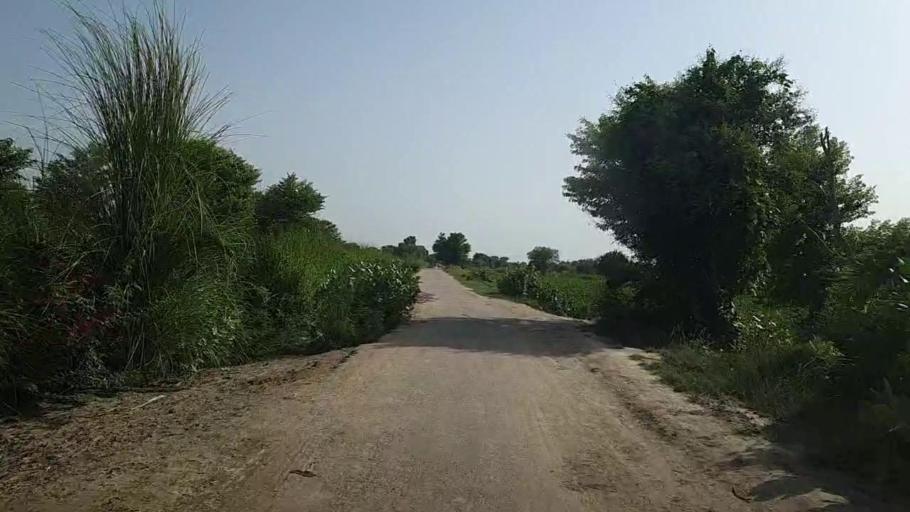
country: PK
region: Sindh
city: Karaundi
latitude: 26.8606
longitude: 68.3654
